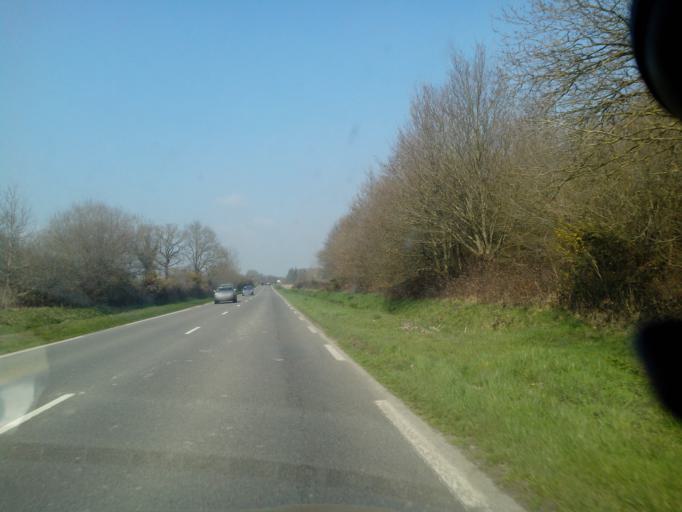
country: FR
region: Brittany
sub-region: Departement d'Ille-et-Vilaine
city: Saint-Meen-le-Grand
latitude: 48.2175
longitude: -2.1771
